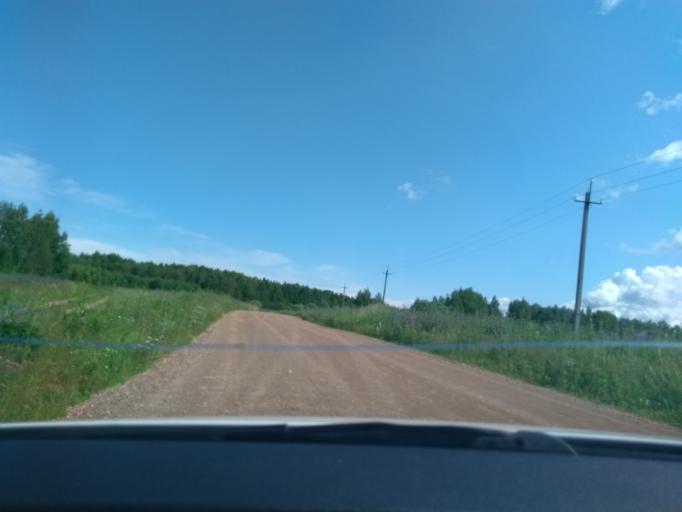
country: RU
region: Perm
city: Sylva
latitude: 57.8243
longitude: 56.7469
